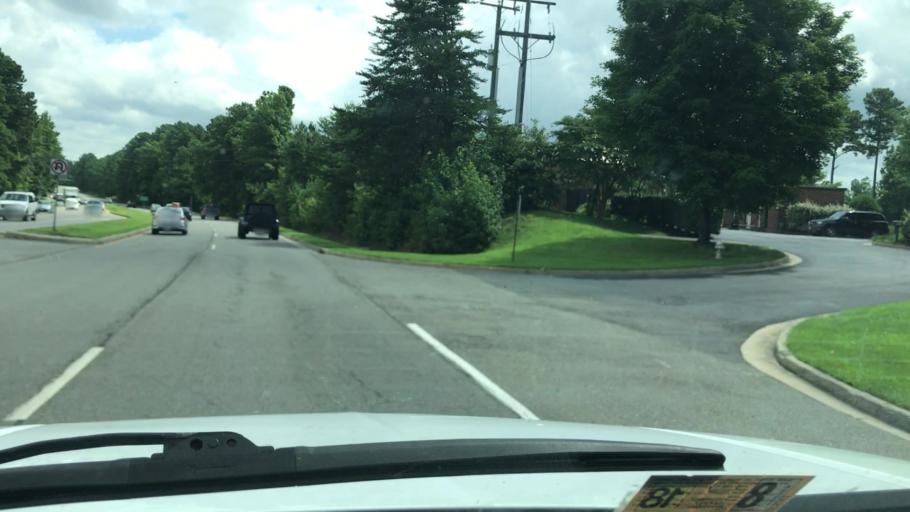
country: US
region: Virginia
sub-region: Henrico County
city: Laurel
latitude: 37.6361
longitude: -77.4970
